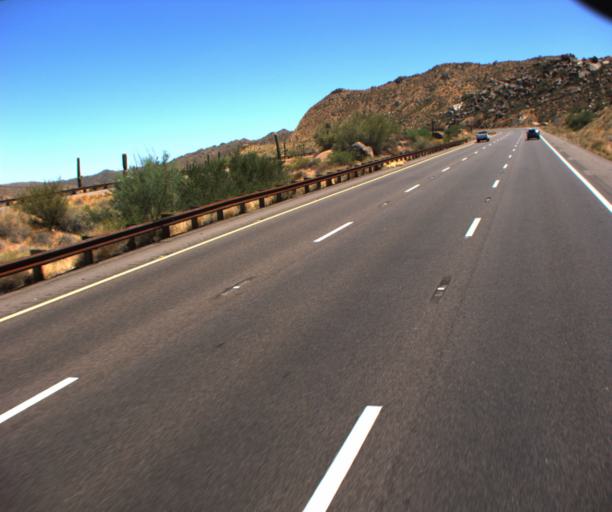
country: US
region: Arizona
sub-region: Maricopa County
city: Rio Verde
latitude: 33.7162
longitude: -111.5109
